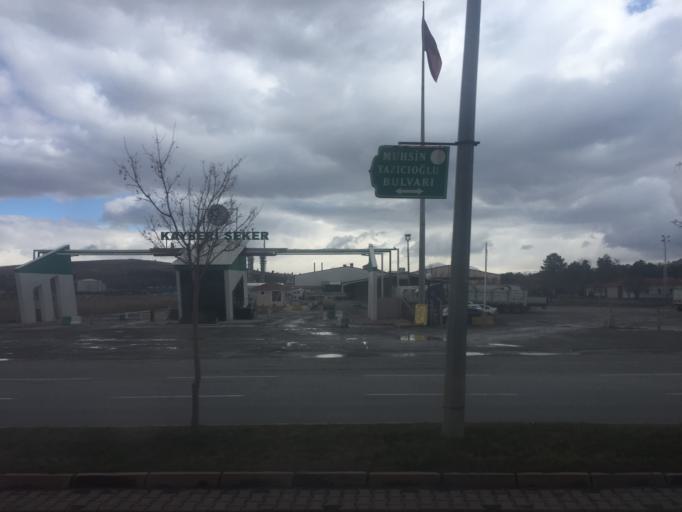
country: TR
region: Kayseri
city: Melikgazi
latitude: 38.7524
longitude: 35.4066
